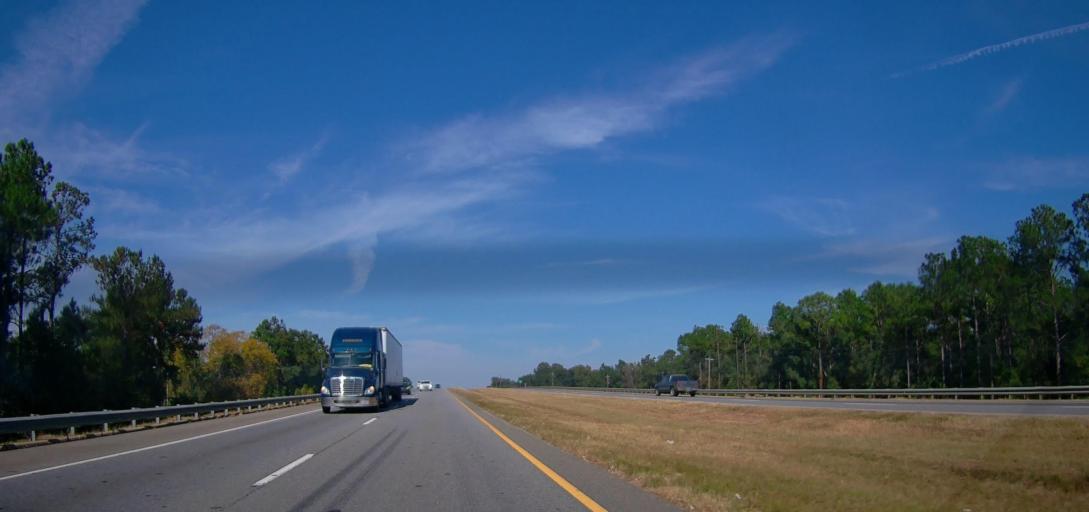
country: US
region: Georgia
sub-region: Dougherty County
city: Albany
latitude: 31.5609
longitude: -84.1141
